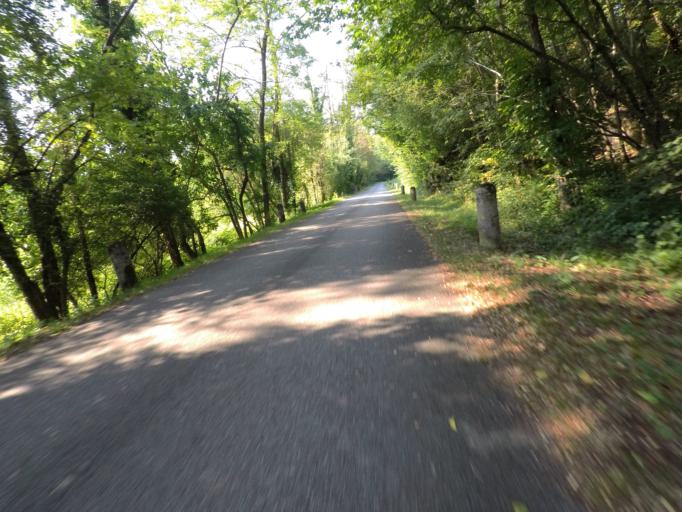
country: IT
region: Friuli Venezia Giulia
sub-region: Provincia di Pordenone
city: Pinzano al Tagliamento
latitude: 46.1942
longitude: 12.9553
